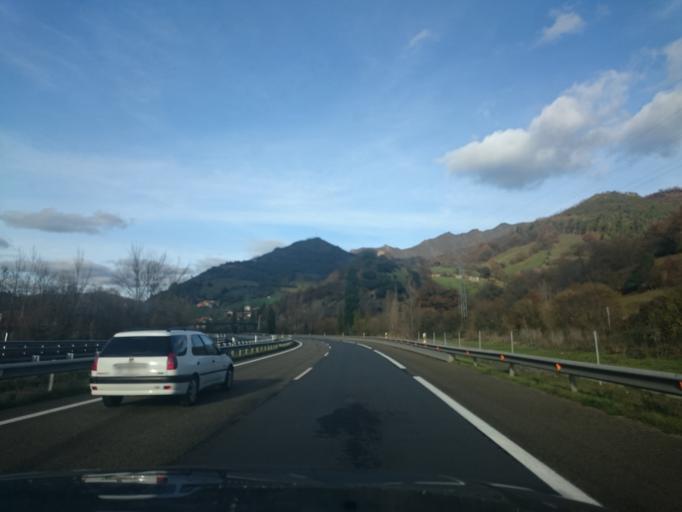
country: ES
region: Asturias
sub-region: Province of Asturias
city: Pola de Lena
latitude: 43.1244
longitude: -5.8158
